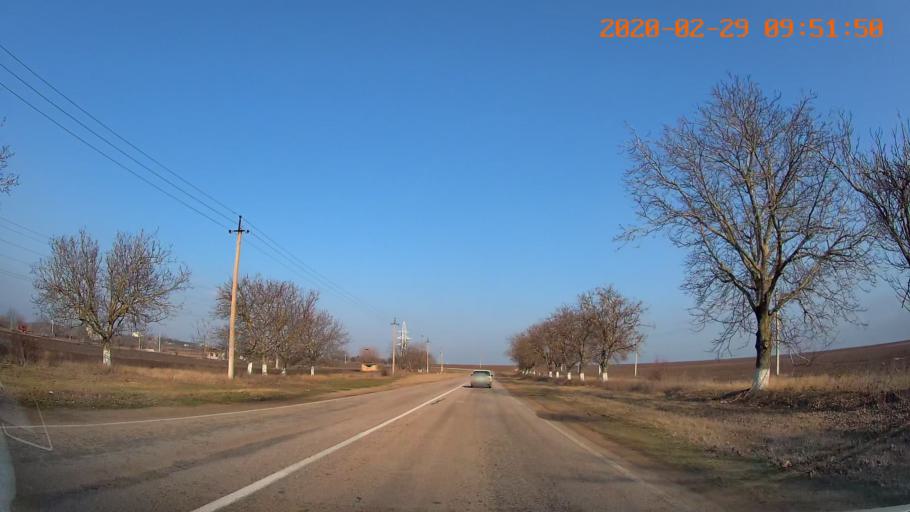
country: MD
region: Telenesti
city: Slobozia
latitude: 46.7118
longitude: 29.7353
